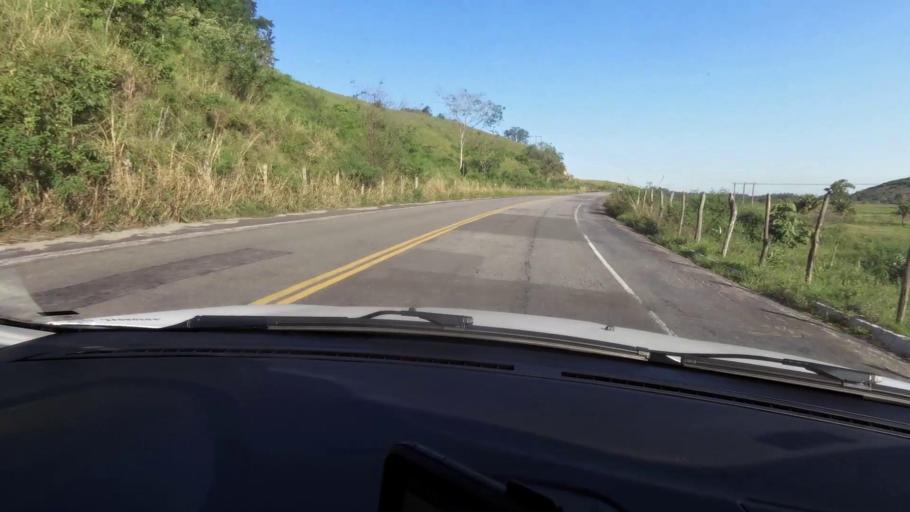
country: BR
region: Espirito Santo
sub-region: Piuma
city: Piuma
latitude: -20.7277
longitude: -40.6538
